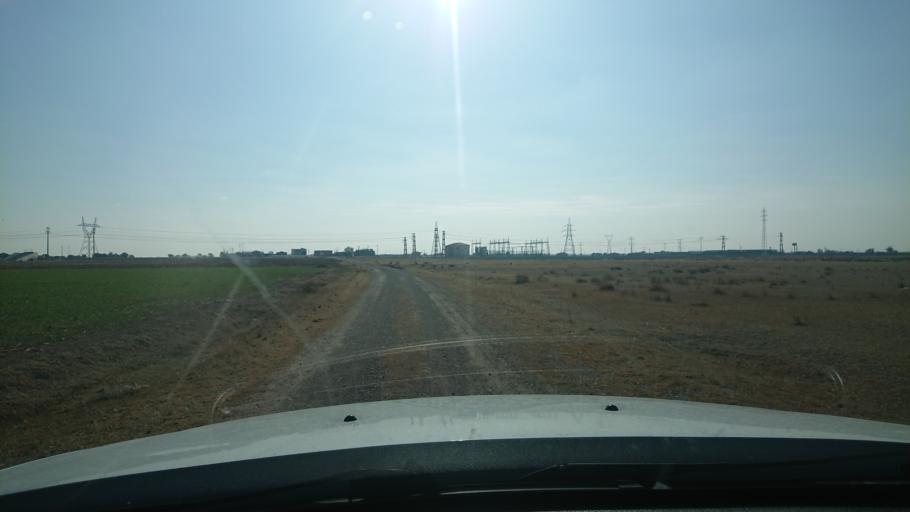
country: TR
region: Aksaray
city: Sultanhani
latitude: 38.2571
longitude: 33.4716
